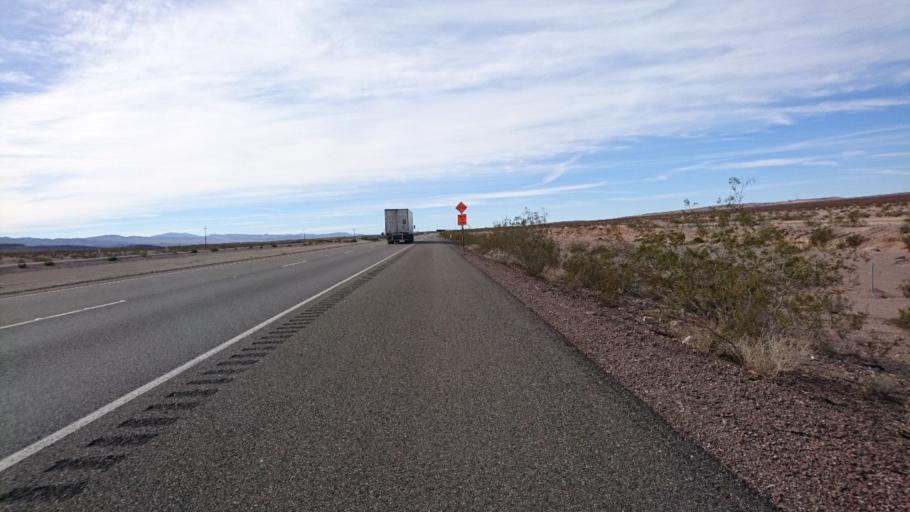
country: US
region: California
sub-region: San Bernardino County
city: Joshua Tree
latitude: 34.7295
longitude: -116.2669
